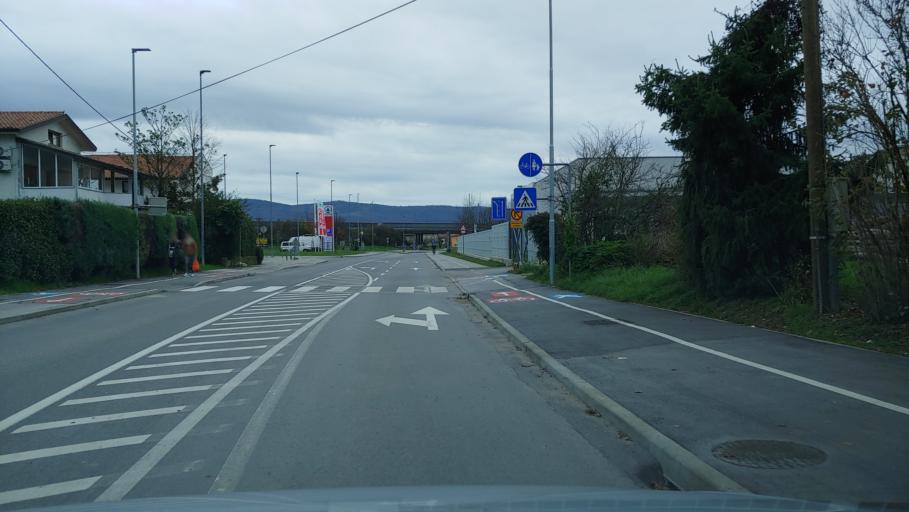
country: SI
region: Sempeter-Vrtojba
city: Sempeter pri Gorici
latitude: 45.9233
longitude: 13.6407
